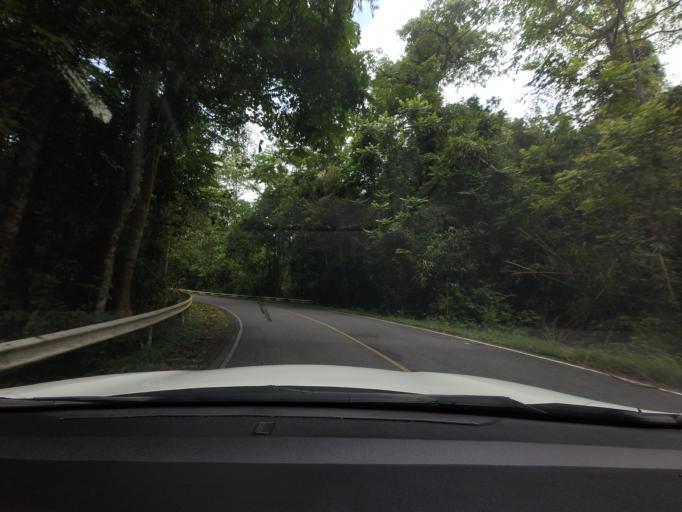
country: TH
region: Nakhon Nayok
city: Pak Phli
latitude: 14.2668
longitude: 101.3878
